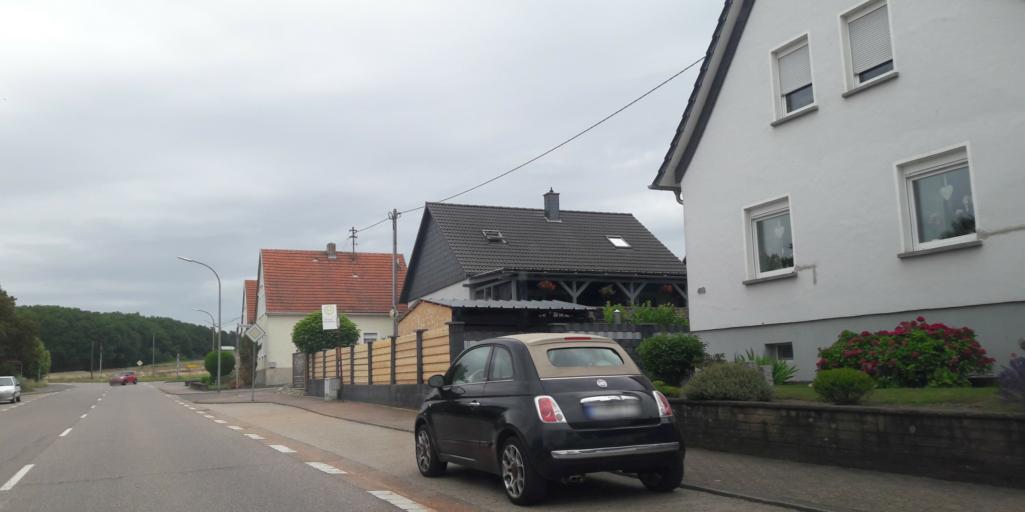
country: DE
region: Saarland
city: Schwalbach
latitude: 49.3093
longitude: 6.8330
